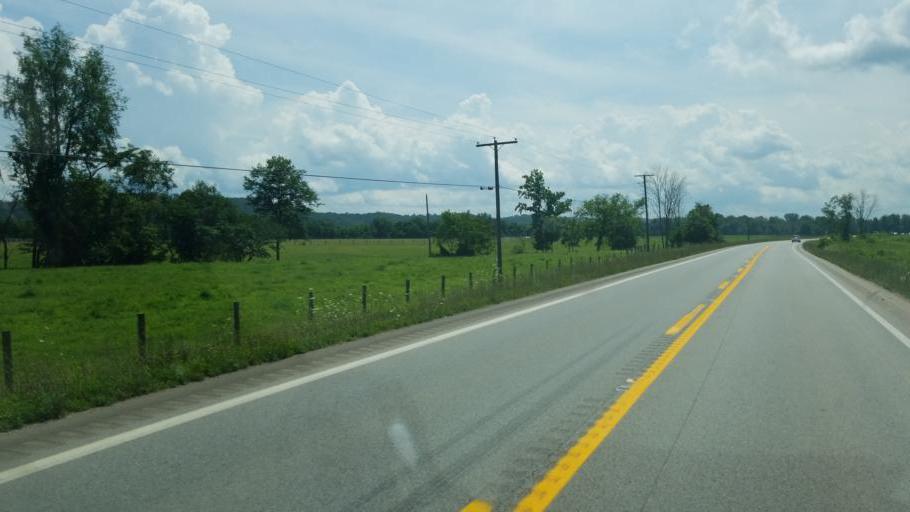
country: US
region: West Virginia
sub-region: Putnam County
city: Buffalo
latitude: 38.6334
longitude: -81.9782
